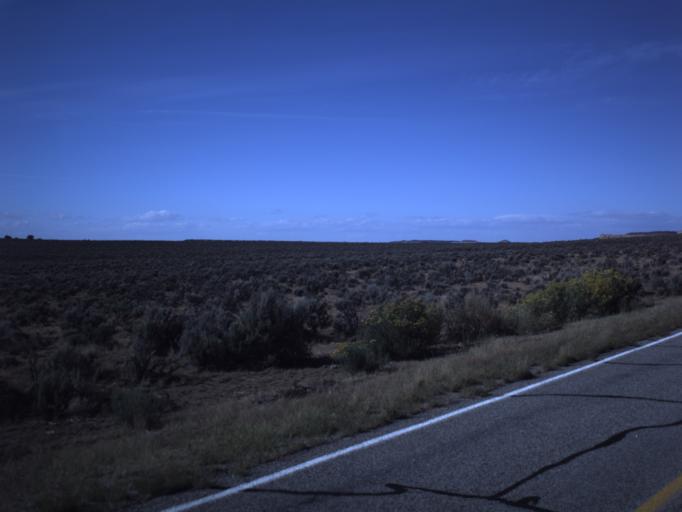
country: US
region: Utah
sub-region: San Juan County
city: Monticello
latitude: 38.0403
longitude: -109.4149
